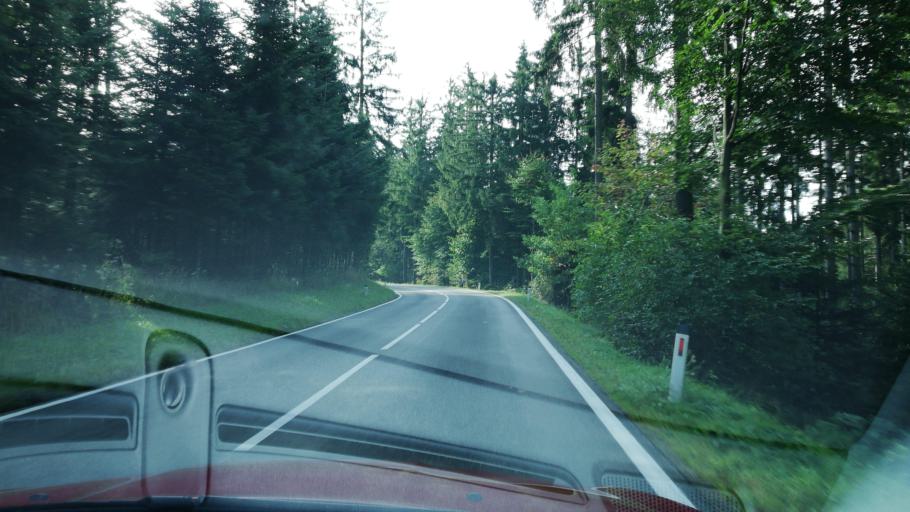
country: AT
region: Upper Austria
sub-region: Politischer Bezirk Vocklabruck
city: Redleiten
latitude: 48.1147
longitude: 13.5597
